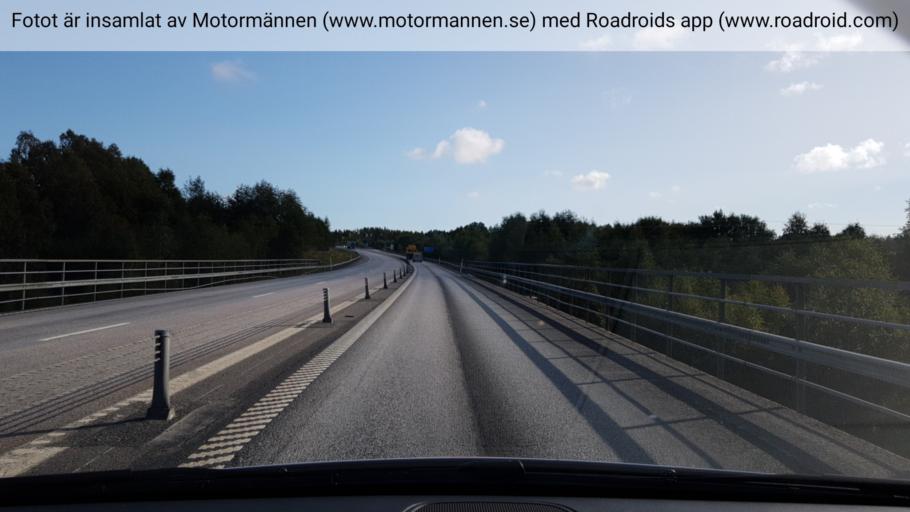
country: SE
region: Vaesterbotten
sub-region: Umea Kommun
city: Saevar
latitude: 63.8967
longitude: 20.5542
